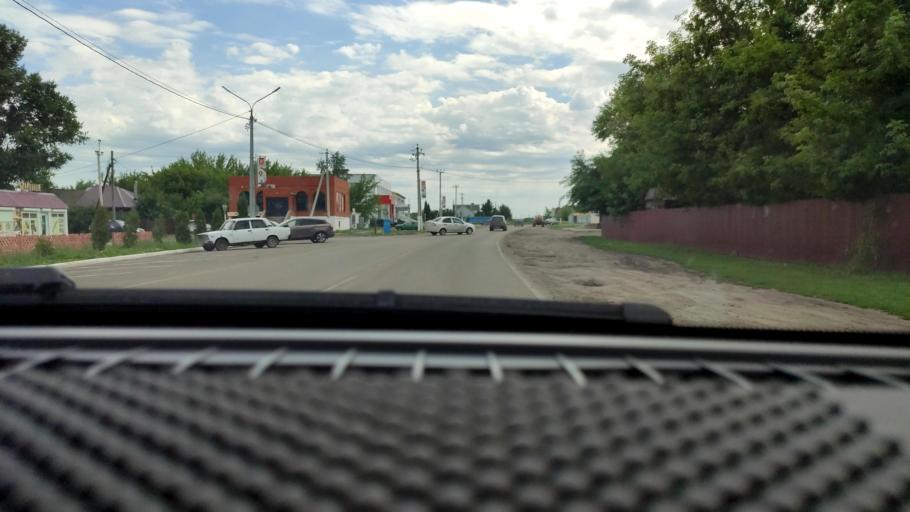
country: RU
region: Voronezj
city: Panino
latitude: 51.6447
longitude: 40.1312
